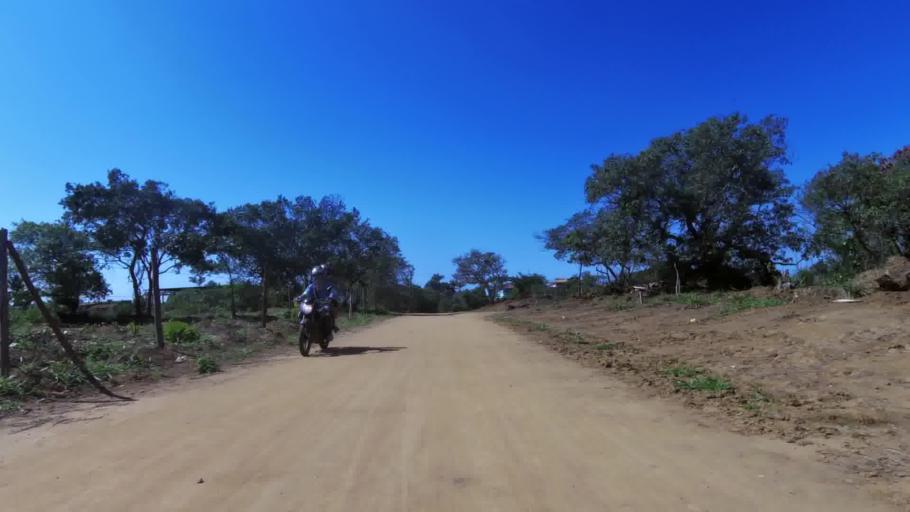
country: BR
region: Espirito Santo
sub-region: Guarapari
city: Guarapari
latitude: -20.7345
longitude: -40.5509
